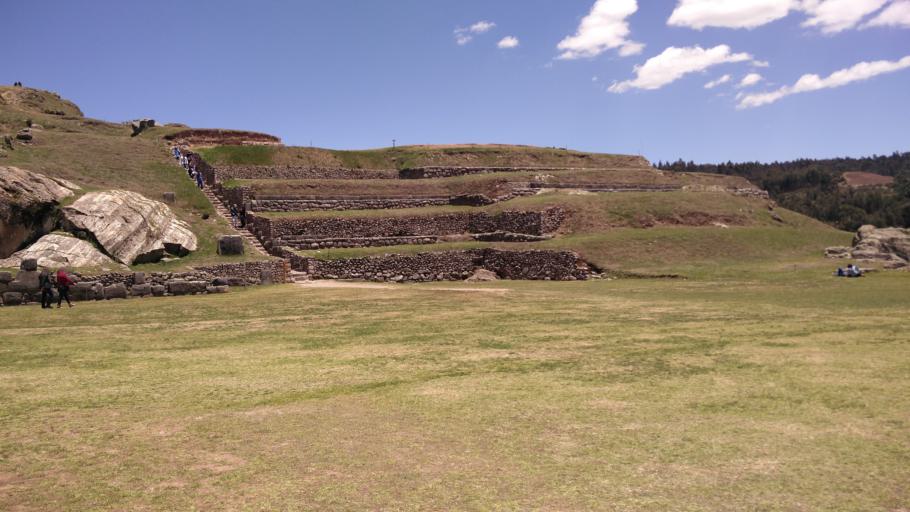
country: PE
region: Cusco
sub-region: Provincia de Cusco
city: Cusco
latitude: -13.5080
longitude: -71.9820
